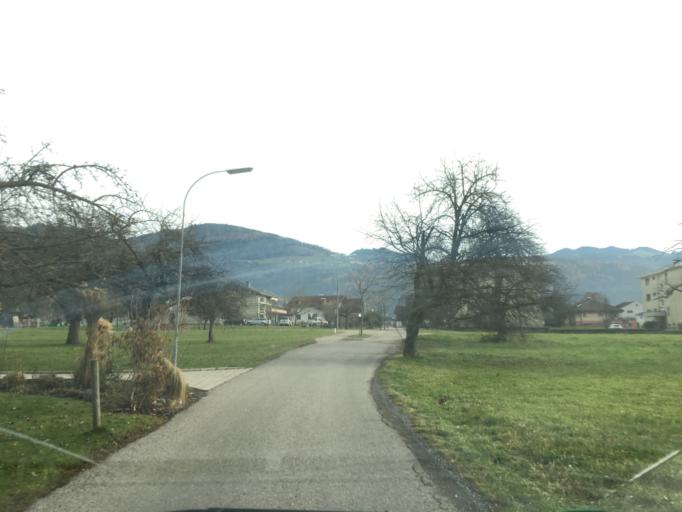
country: AT
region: Vorarlberg
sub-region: Politischer Bezirk Feldkirch
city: Klaus
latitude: 47.3085
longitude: 9.6404
